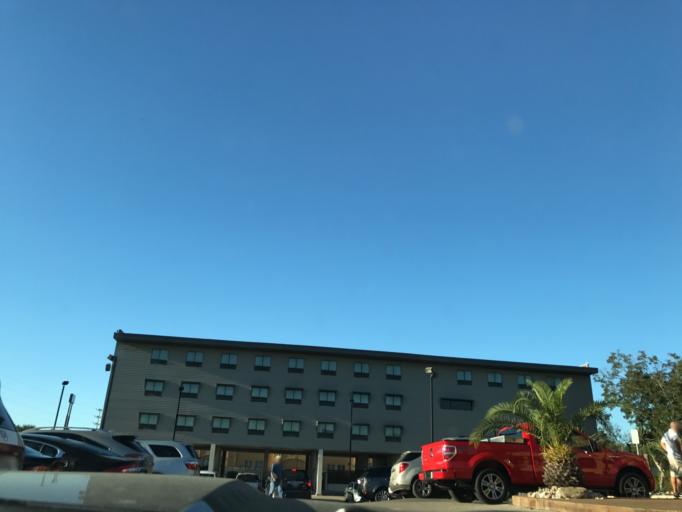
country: US
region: Texas
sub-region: Colorado County
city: Columbus
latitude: 29.6895
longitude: -96.5378
